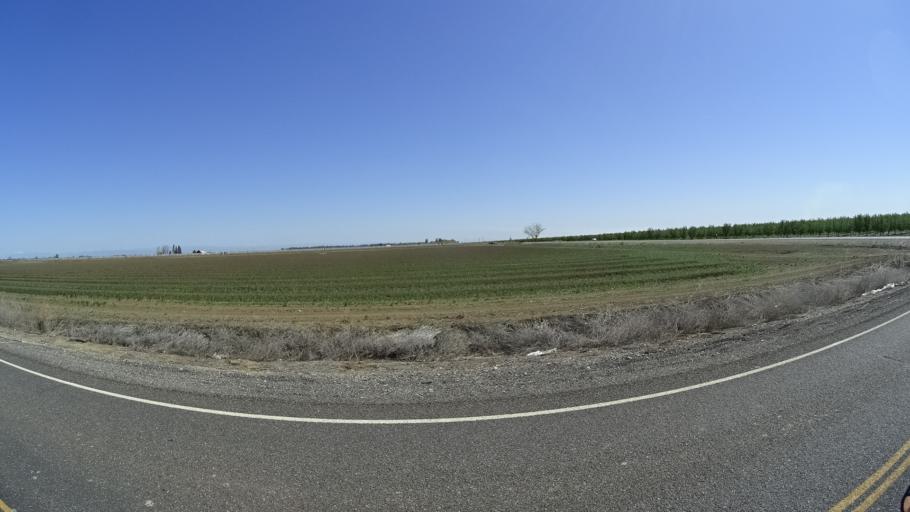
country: US
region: California
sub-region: Glenn County
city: Willows
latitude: 39.5831
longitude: -122.2496
